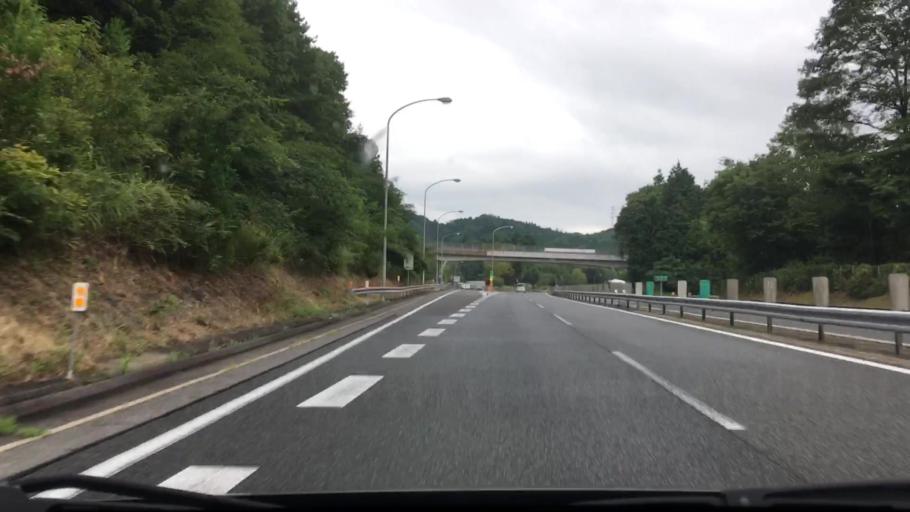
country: JP
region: Hiroshima
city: Miyoshi
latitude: 34.6976
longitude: 132.6026
